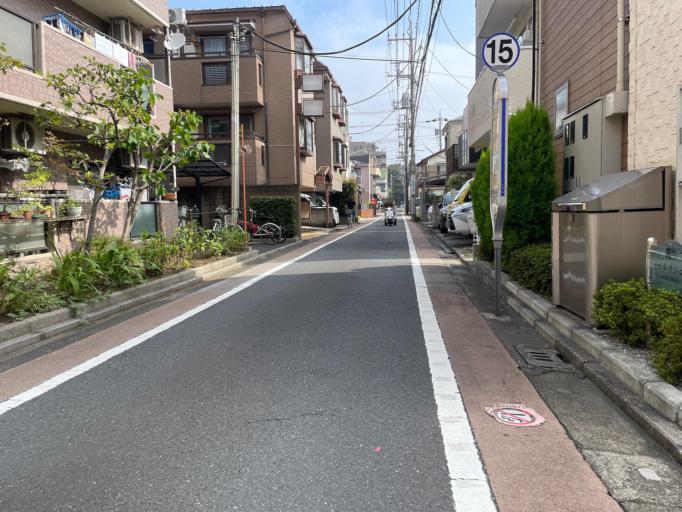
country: JP
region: Tokyo
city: Musashino
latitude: 35.7120
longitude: 139.5589
